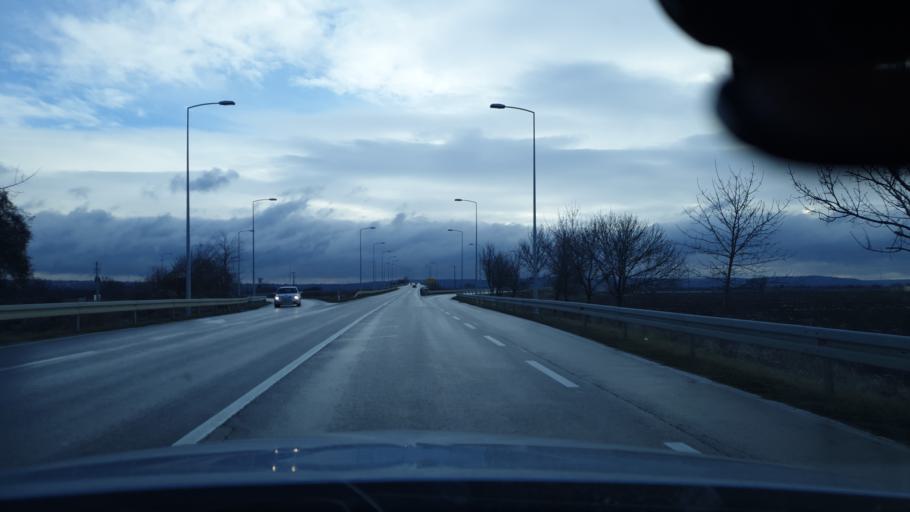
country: RS
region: Central Serbia
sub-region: Branicevski Okrug
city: Pozarevac
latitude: 44.6005
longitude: 21.1457
